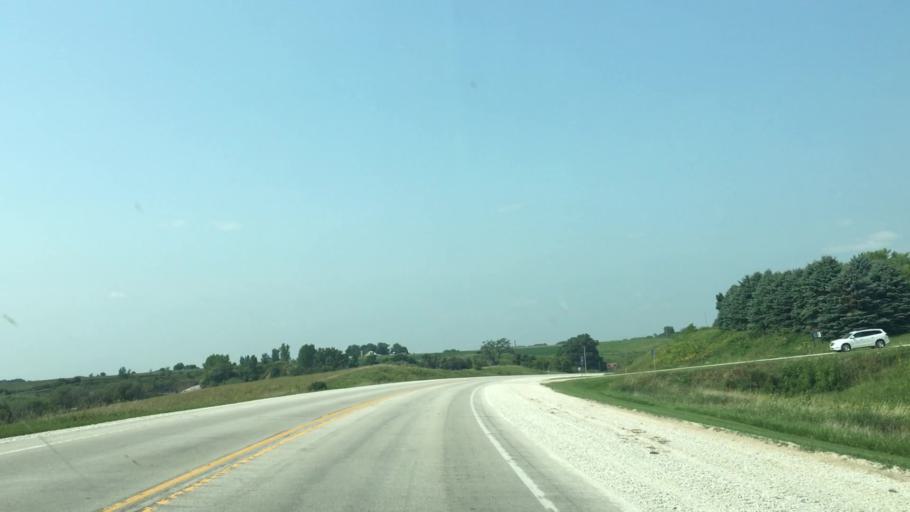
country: US
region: Iowa
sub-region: Winneshiek County
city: Decorah
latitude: 43.4545
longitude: -91.8688
